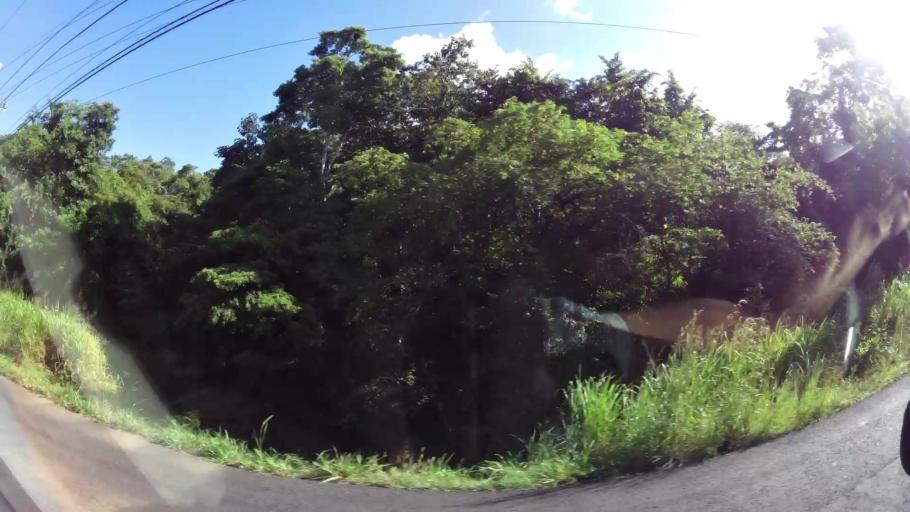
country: CR
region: Guanacaste
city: Sardinal
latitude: 10.5813
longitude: -85.6651
